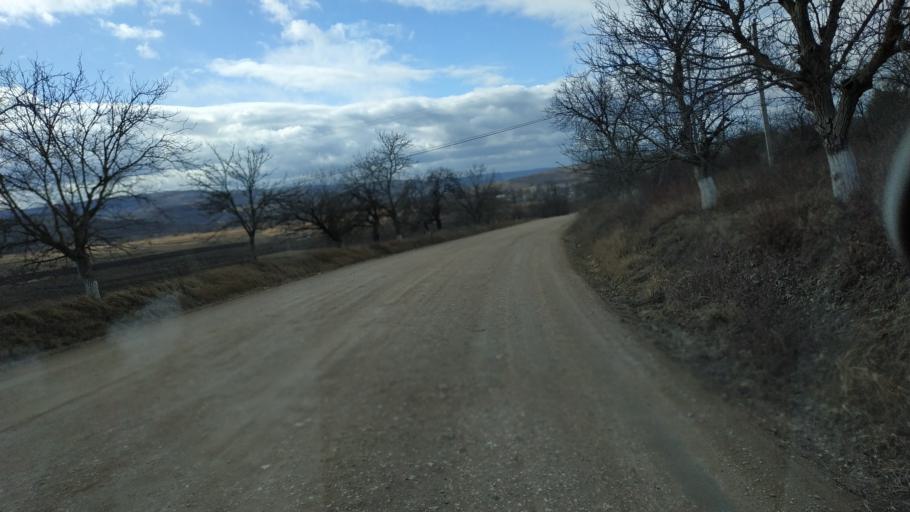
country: MD
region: Stinga Nistrului
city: Bucovat
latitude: 47.1932
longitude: 28.4871
